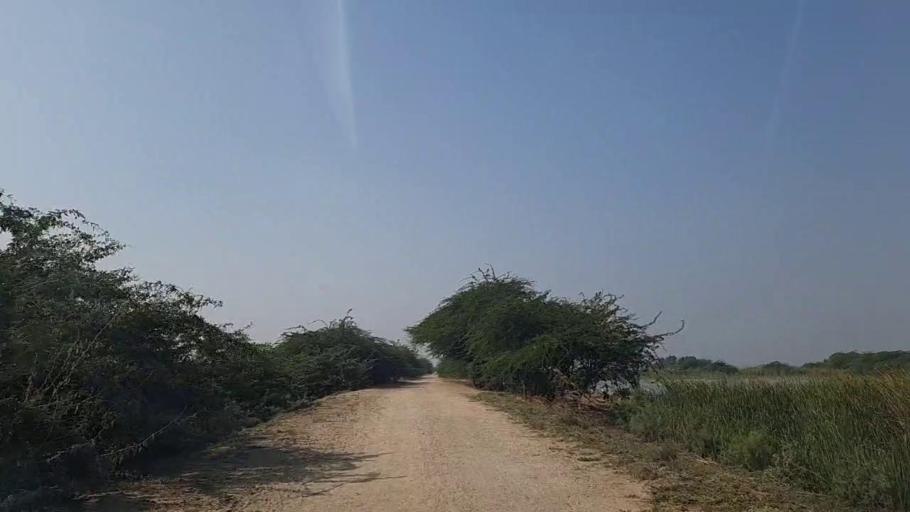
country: PK
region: Sindh
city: Mirpur Sakro
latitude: 24.5749
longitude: 67.7736
